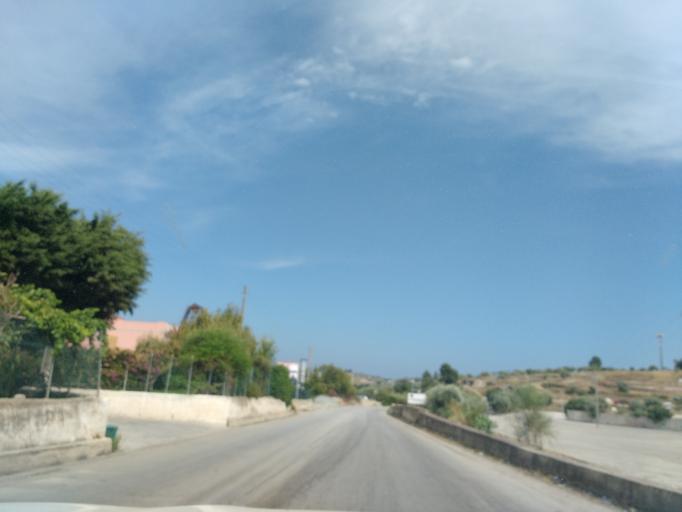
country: IT
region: Sicily
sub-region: Provincia di Siracusa
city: Noto
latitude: 36.8812
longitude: 15.0647
